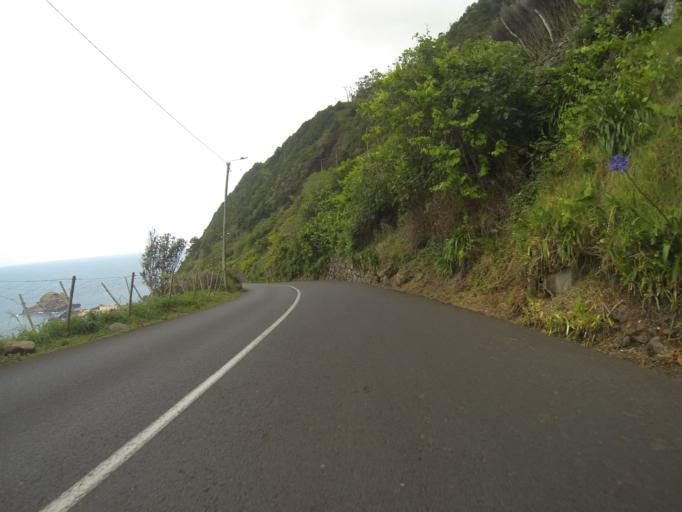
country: PT
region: Madeira
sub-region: Porto Moniz
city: Porto Moniz
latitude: 32.8639
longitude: -17.1733
